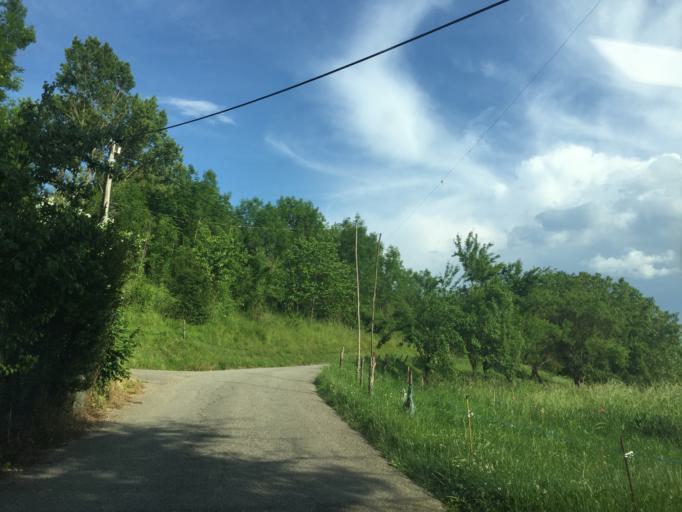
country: FR
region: Rhone-Alpes
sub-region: Departement de la Savoie
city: Drumettaz-Clarafond
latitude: 45.6664
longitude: 5.9274
